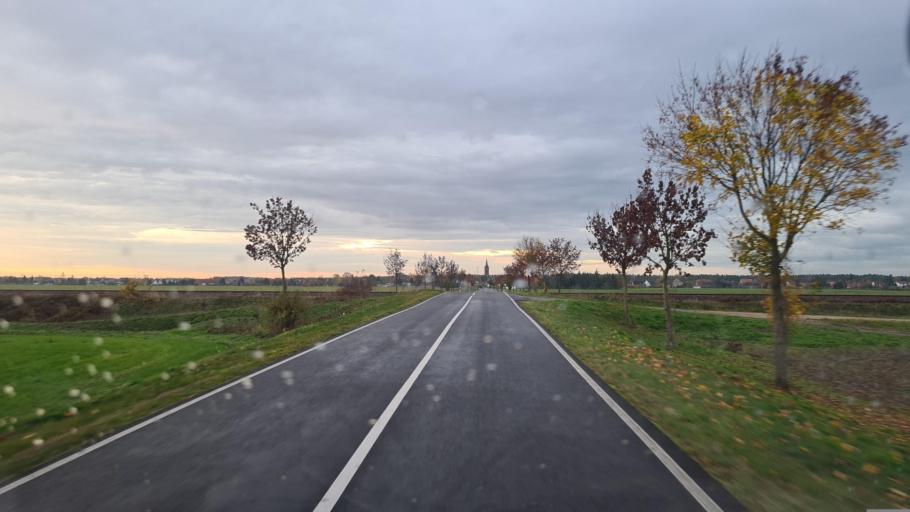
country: DE
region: Saxony-Anhalt
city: Holzdorf
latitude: 51.7863
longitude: 13.1306
